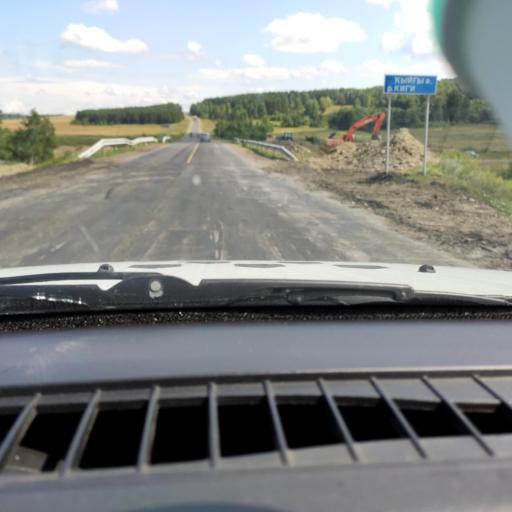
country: RU
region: Bashkortostan
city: Verkhniye Kigi
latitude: 55.3213
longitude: 58.7088
